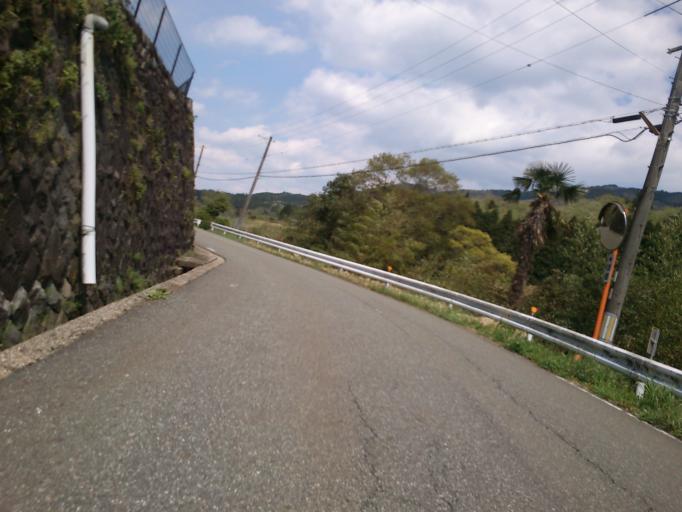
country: JP
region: Hyogo
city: Toyooka
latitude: 35.3921
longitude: 134.9422
